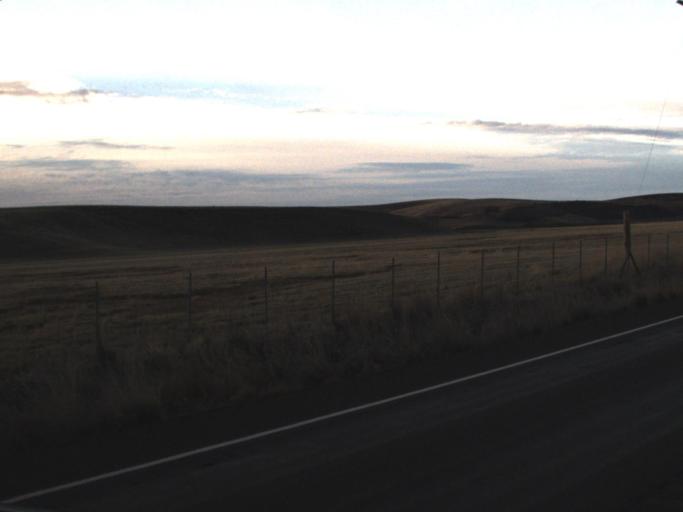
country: US
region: Washington
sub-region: Whitman County
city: Colfax
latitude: 46.8020
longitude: -117.6655
